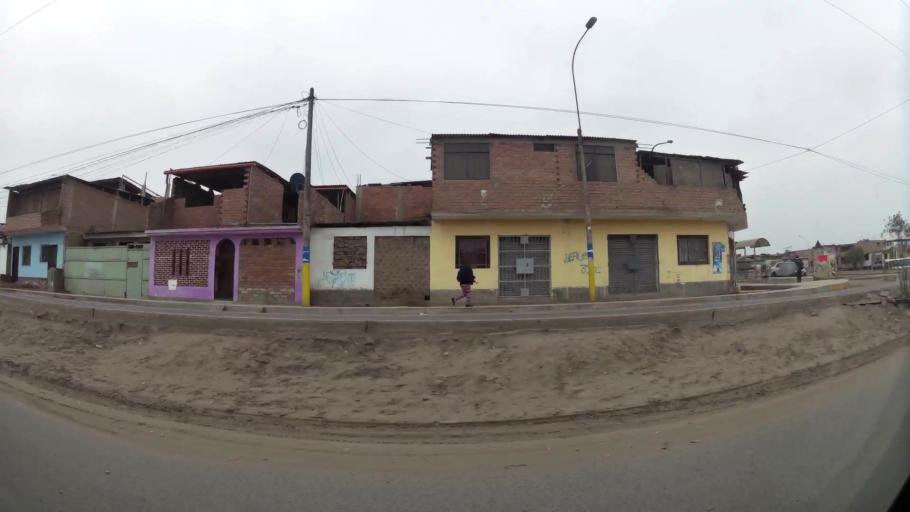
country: PE
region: Lima
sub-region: Lima
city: Surco
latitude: -12.2192
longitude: -76.9299
